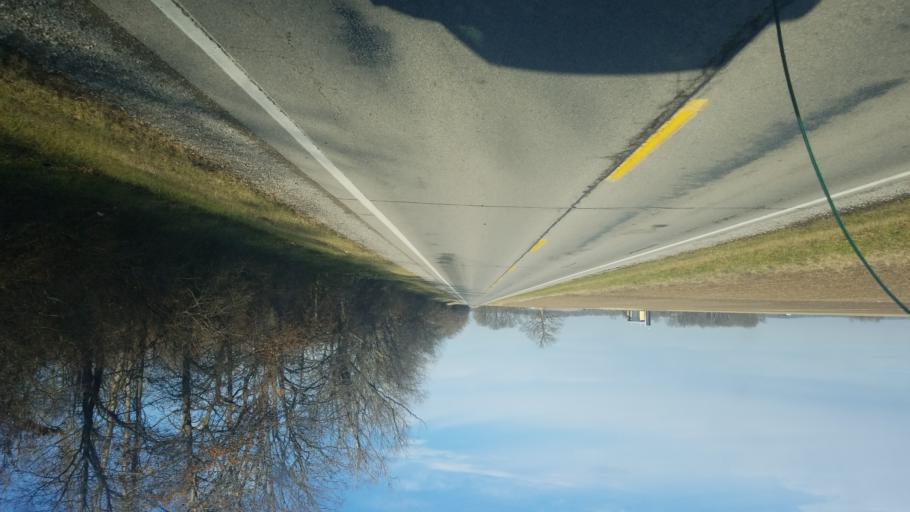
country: US
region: Illinois
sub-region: Wabash County
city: Mount Carmel
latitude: 38.3641
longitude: -87.8521
